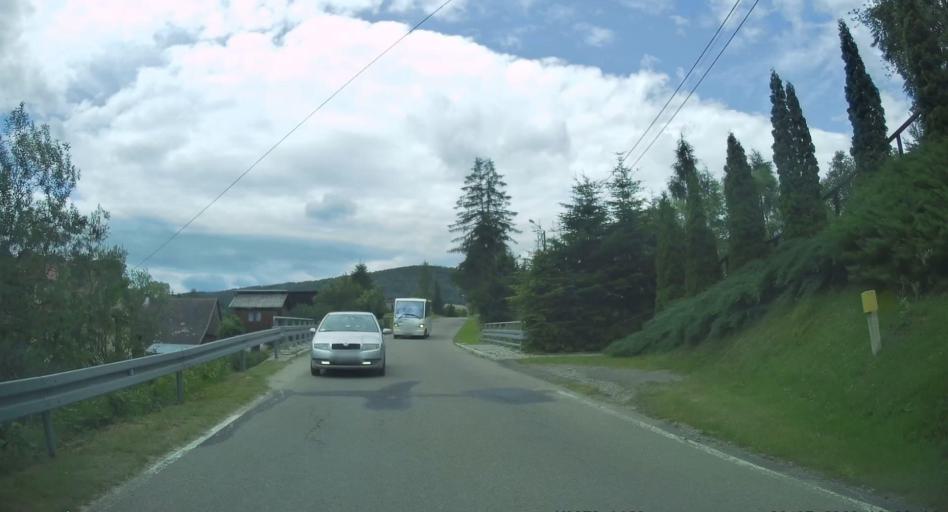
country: PL
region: Lesser Poland Voivodeship
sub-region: Powiat nowosadecki
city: Muszyna
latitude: 49.3855
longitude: 20.9159
